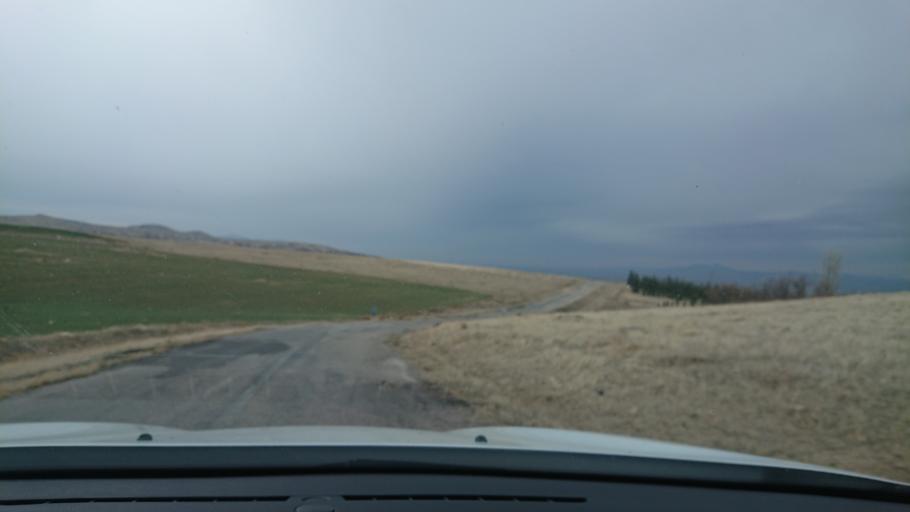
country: TR
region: Aksaray
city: Sariyahsi
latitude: 38.9487
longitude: 33.9031
